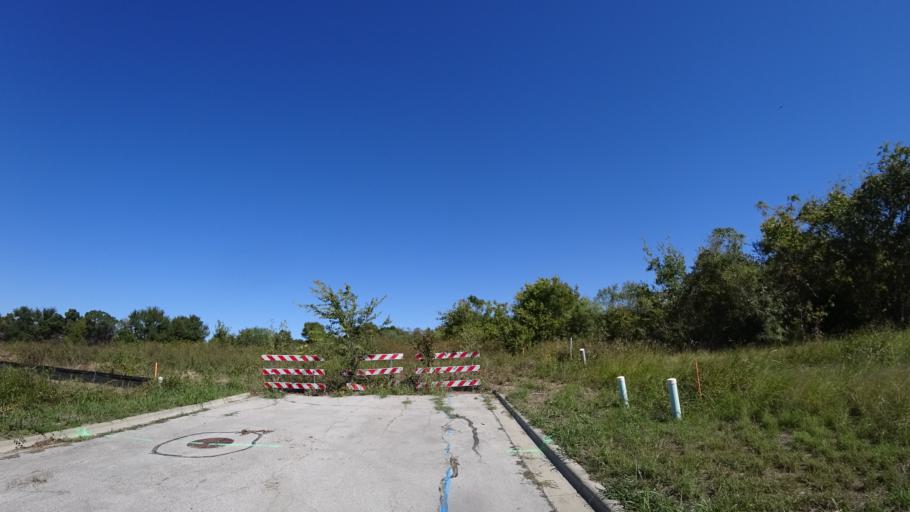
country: US
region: Texas
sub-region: Travis County
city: Hornsby Bend
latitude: 30.3056
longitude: -97.6465
